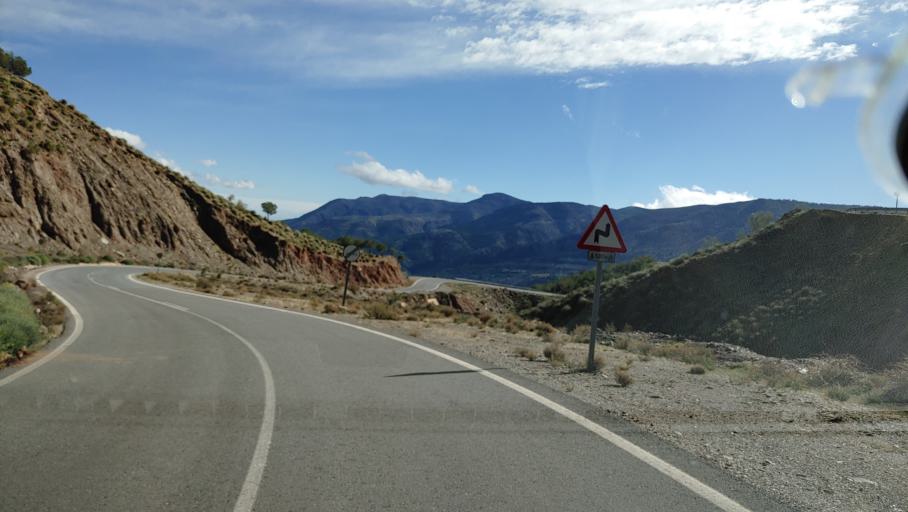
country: ES
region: Andalusia
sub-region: Provincia de Almeria
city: Canjayar
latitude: 37.0213
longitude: -2.7259
